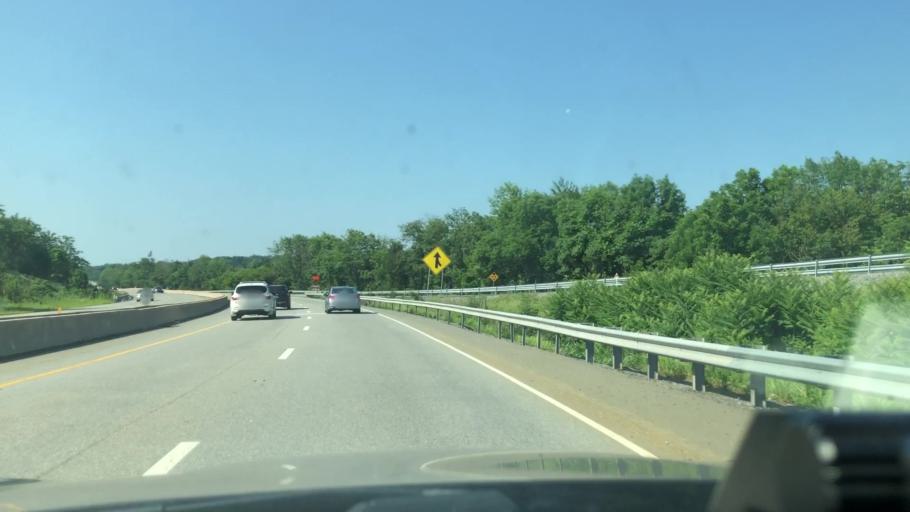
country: US
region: Pennsylvania
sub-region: Montgomery County
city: Halfway House
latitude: 40.2889
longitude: -75.6425
